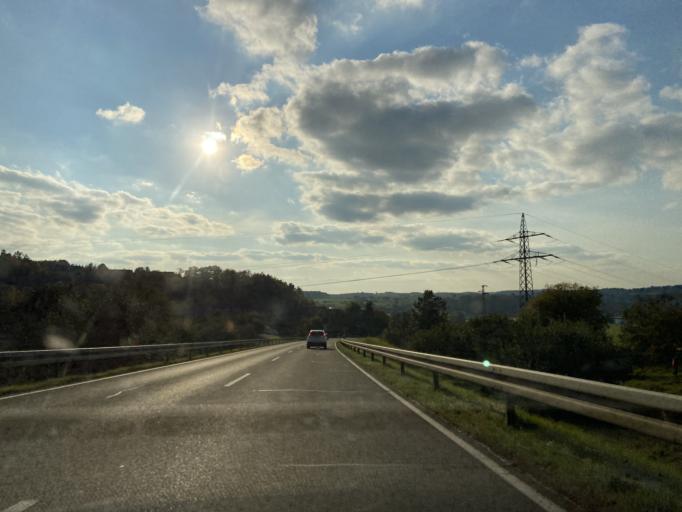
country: DE
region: Baden-Wuerttemberg
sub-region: Tuebingen Region
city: Bingen
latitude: 48.1070
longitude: 9.2980
